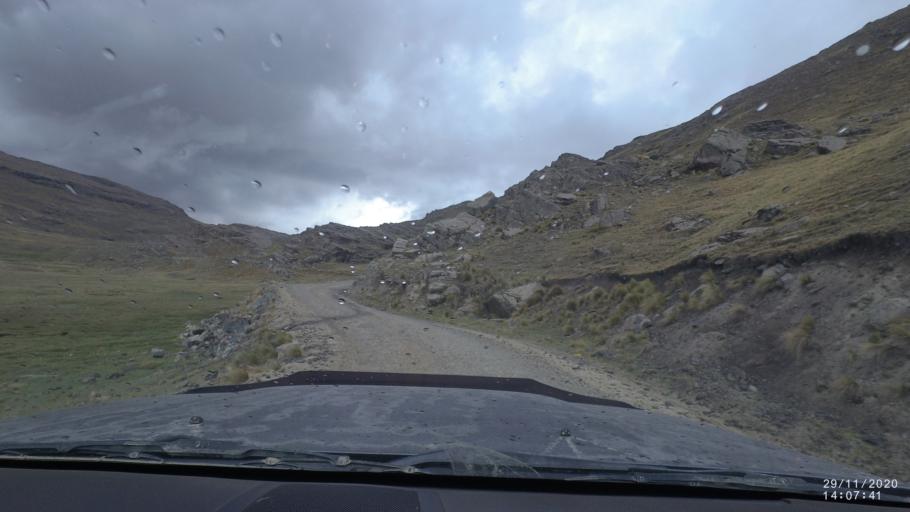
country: BO
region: Cochabamba
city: Sipe Sipe
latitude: -17.2195
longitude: -66.3841
